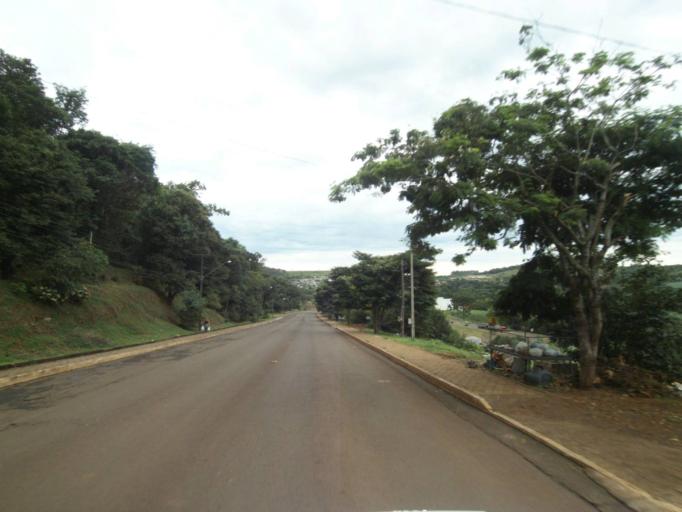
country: BR
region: Parana
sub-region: Guaraniacu
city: Guaraniacu
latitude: -25.1067
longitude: -52.8579
